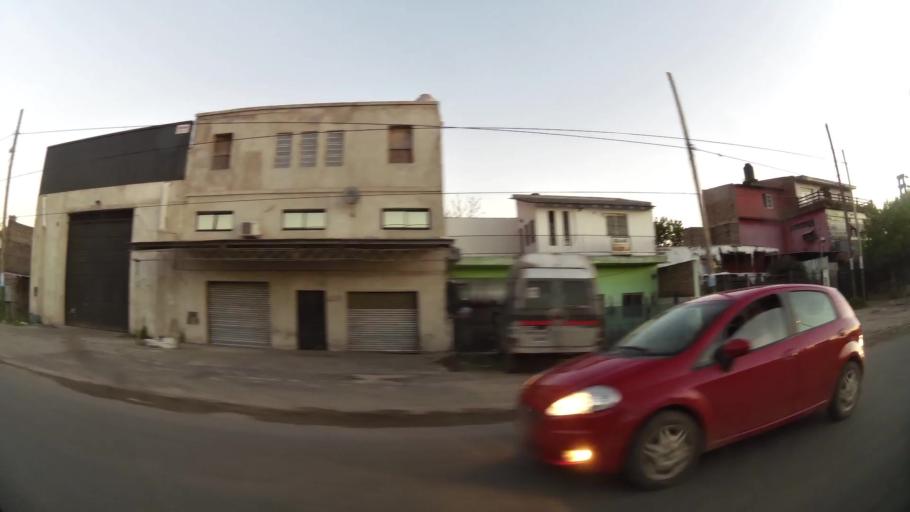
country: AR
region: Buenos Aires
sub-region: Partido de Almirante Brown
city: Adrogue
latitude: -34.7944
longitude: -58.3171
